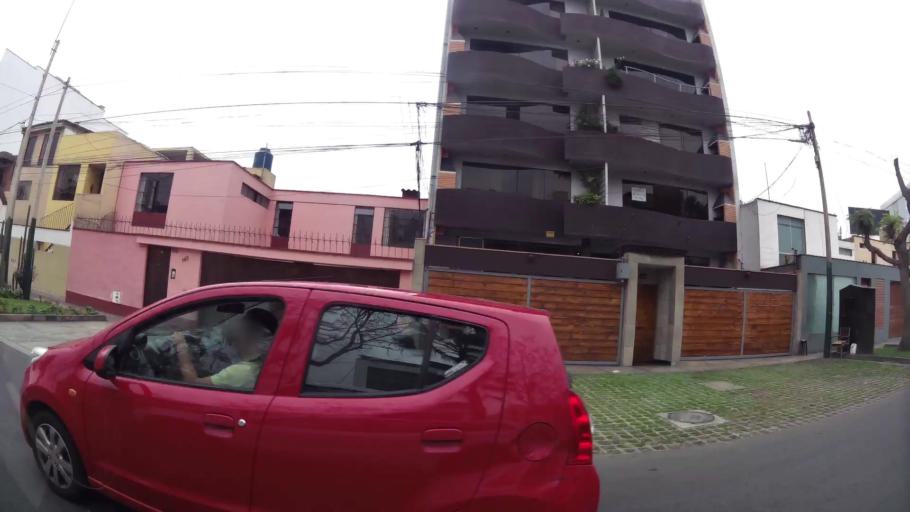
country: PE
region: Lima
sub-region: Lima
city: Surco
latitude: -12.1287
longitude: -76.9880
